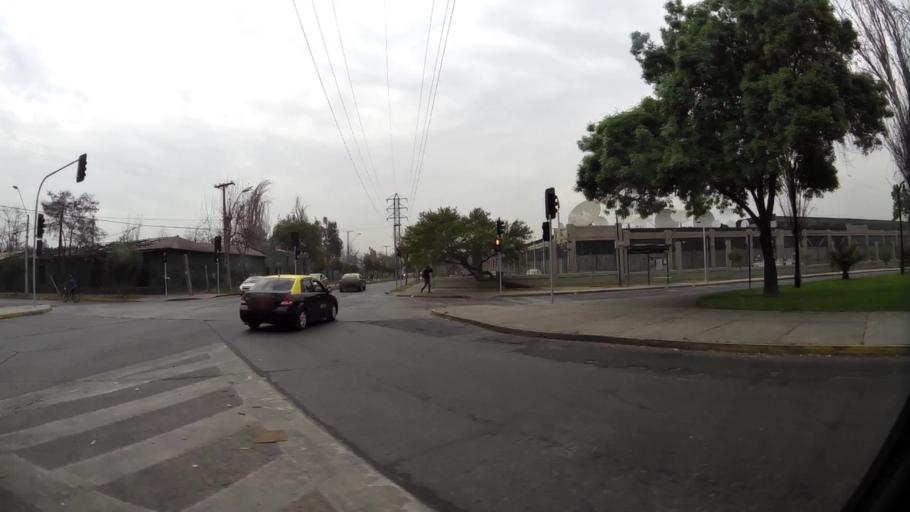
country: CL
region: Santiago Metropolitan
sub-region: Provincia de Santiago
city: Santiago
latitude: -33.4736
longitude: -70.6650
